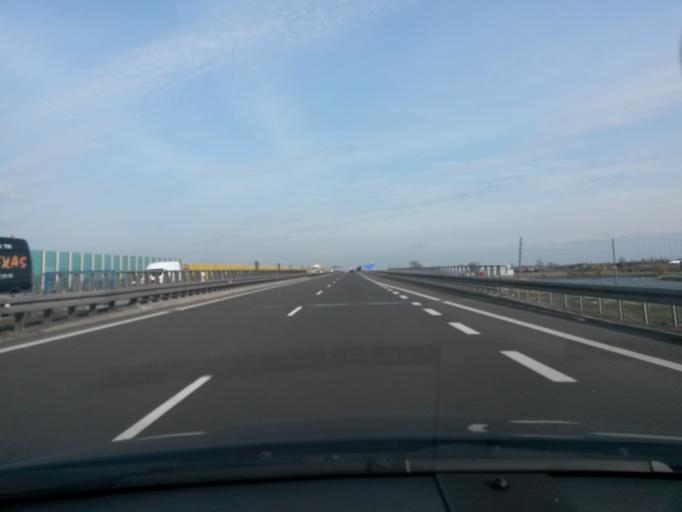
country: PL
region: Greater Poland Voivodeship
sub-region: Powiat wrzesinski
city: Wrzesnia
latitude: 52.3141
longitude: 17.5396
